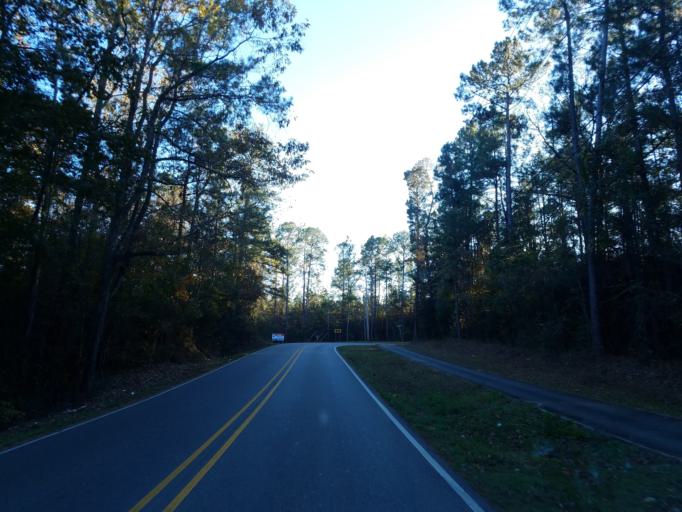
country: US
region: Mississippi
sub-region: Lamar County
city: Arnold Line
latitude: 31.3473
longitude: -89.3777
